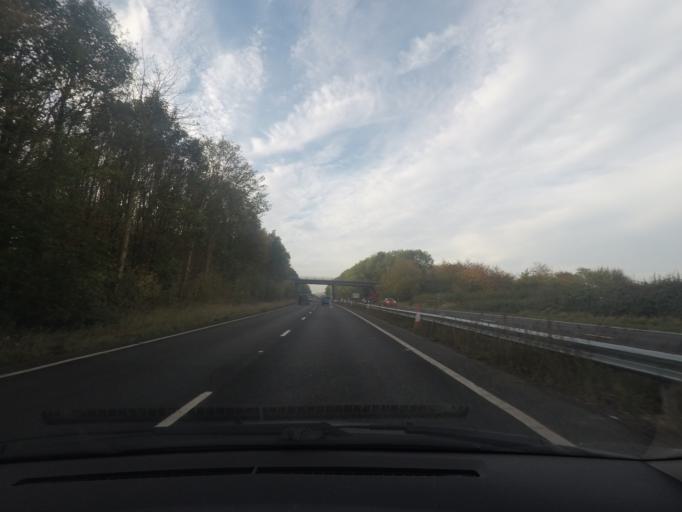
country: GB
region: England
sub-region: North Yorkshire
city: Tadcaster
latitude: 53.8858
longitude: -1.2492
